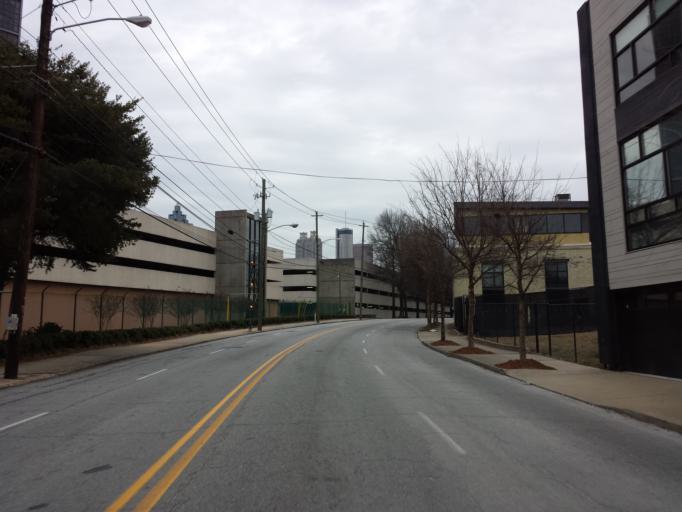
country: US
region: Georgia
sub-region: Fulton County
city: Atlanta
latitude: 33.7703
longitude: -84.3994
